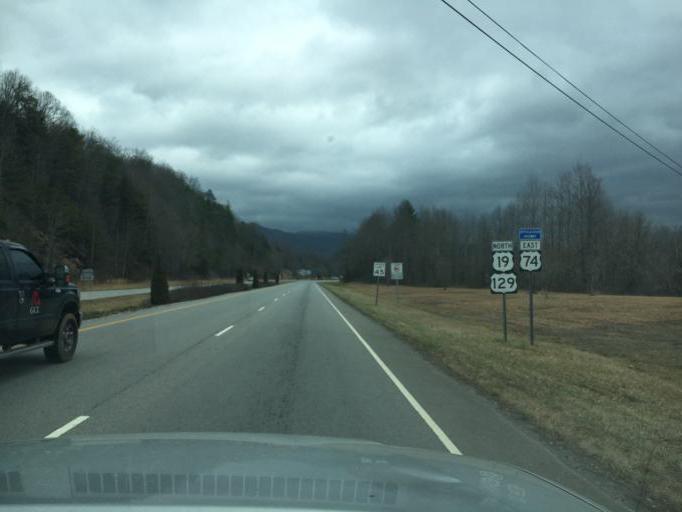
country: US
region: North Carolina
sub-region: Cherokee County
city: Andrews
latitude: 35.2032
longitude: -83.8409
